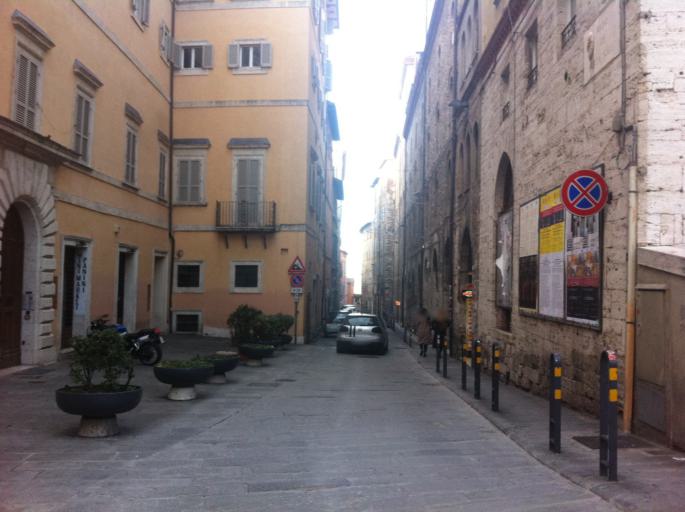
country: IT
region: Umbria
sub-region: Provincia di Perugia
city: Perugia
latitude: 43.1126
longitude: 12.3894
